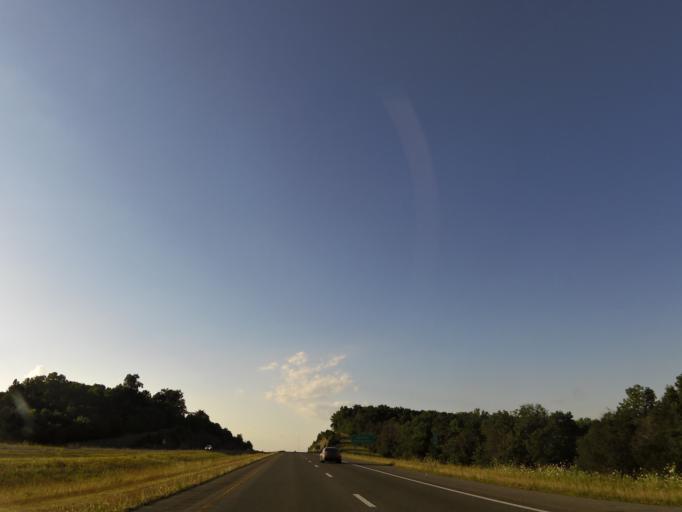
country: US
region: Tennessee
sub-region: Rutherford County
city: Smyrna
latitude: 36.0266
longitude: -86.4282
